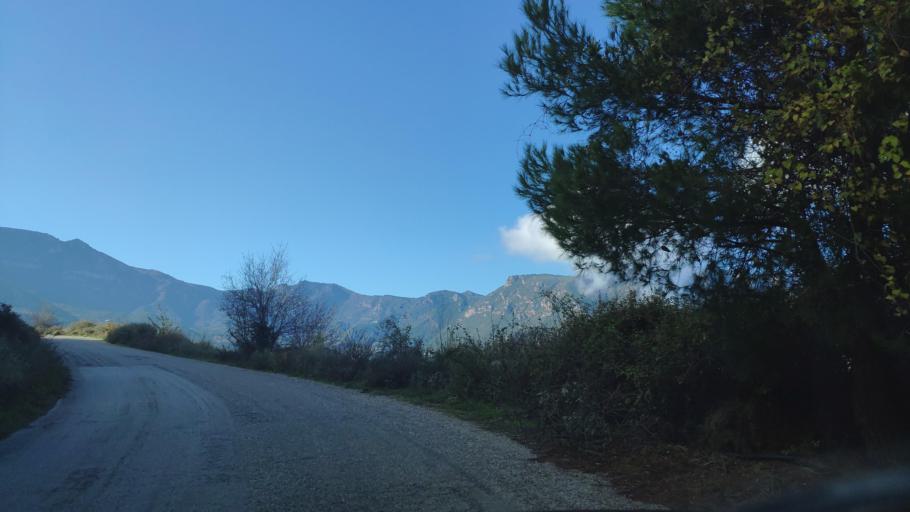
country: GR
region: West Greece
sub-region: Nomos Achaias
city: Aiyira
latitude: 38.0981
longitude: 22.4393
